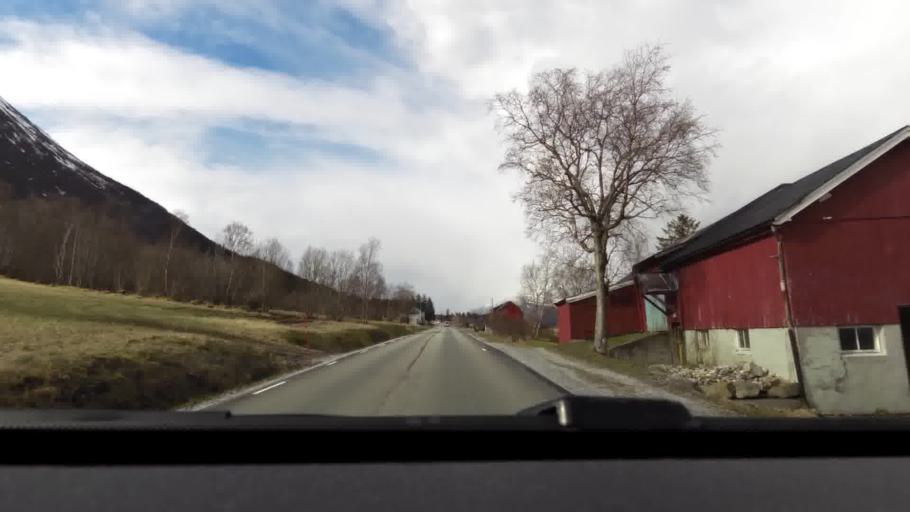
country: NO
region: More og Romsdal
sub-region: Averoy
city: Bruhagen
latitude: 63.1080
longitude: 7.6320
